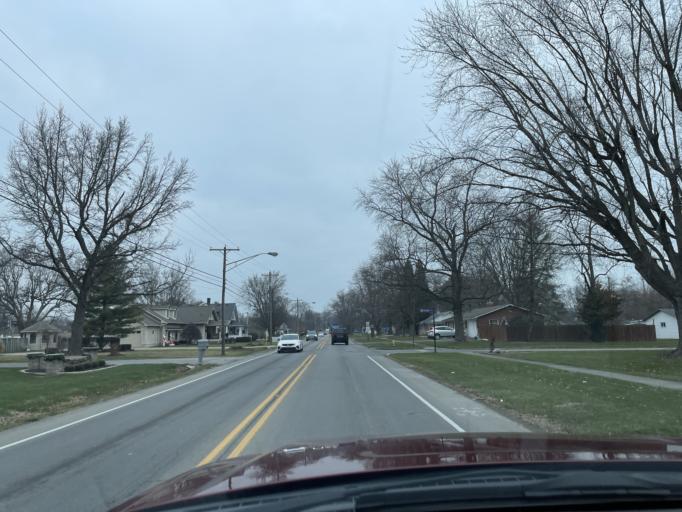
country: US
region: Indiana
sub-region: Hendricks County
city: Brownsburg
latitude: 39.8325
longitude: -86.4012
